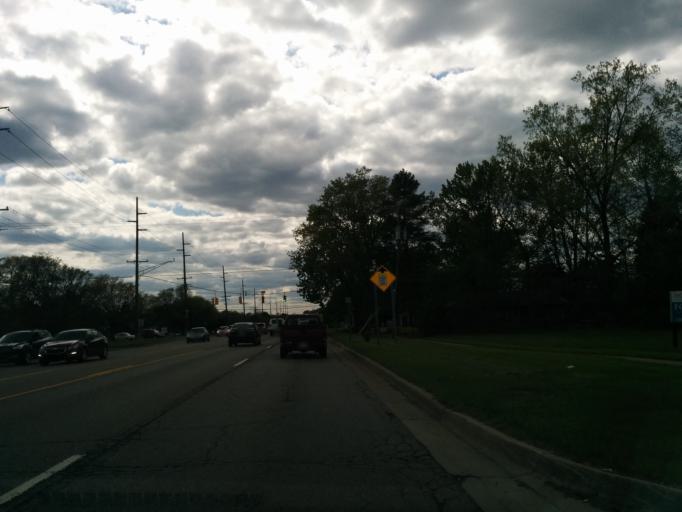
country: US
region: Michigan
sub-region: Oakland County
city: Farmington Hills
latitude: 42.4990
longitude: -83.3686
